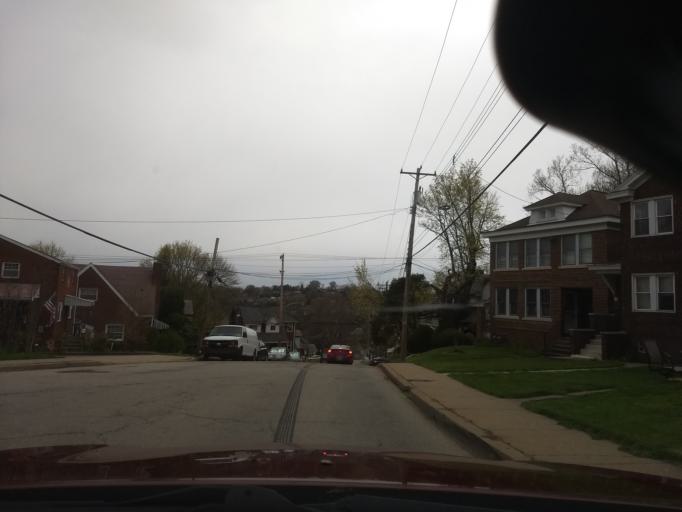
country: US
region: Pennsylvania
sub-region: Allegheny County
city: Dormont
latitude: 40.4003
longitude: -80.0393
